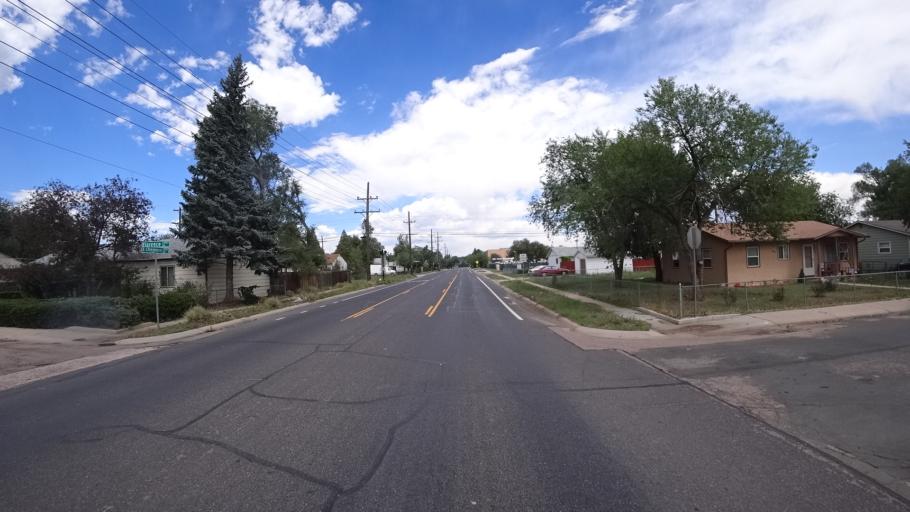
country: US
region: Colorado
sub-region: El Paso County
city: Stratmoor
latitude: 38.7989
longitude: -104.8035
